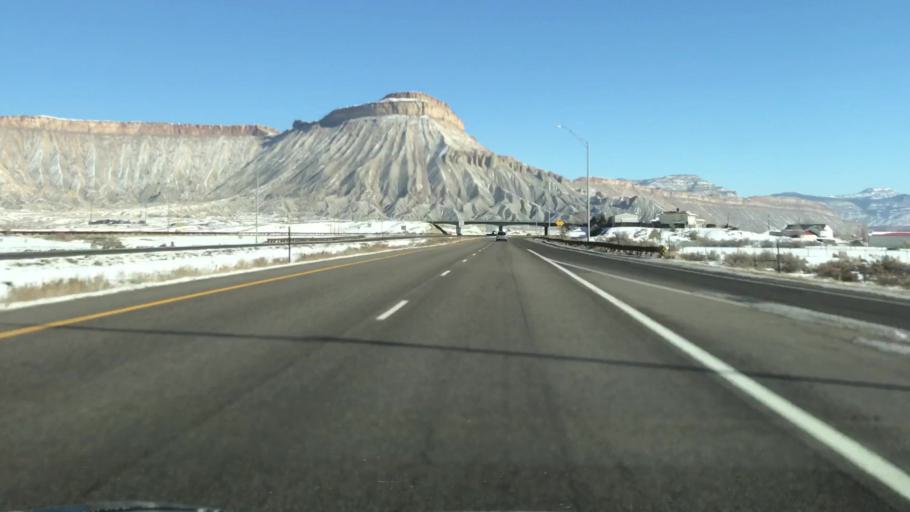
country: US
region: Colorado
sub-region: Mesa County
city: Clifton
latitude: 39.1051
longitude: -108.4449
